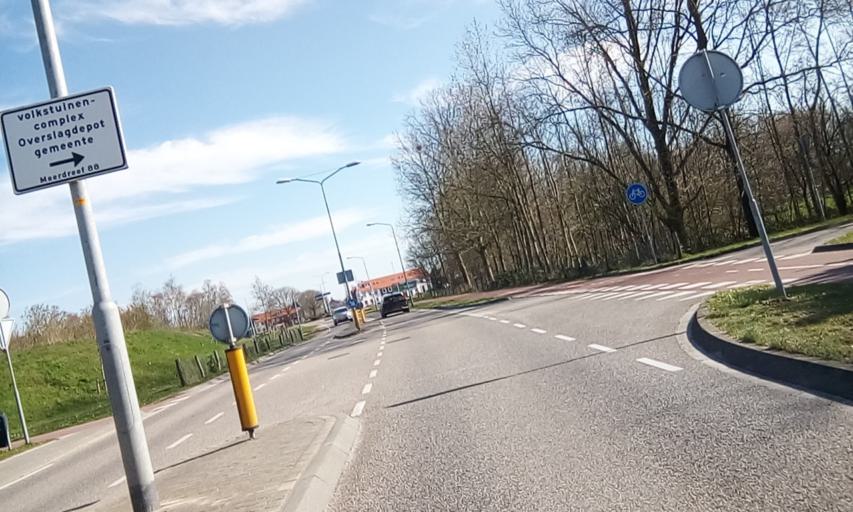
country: NL
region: Gelderland
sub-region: Gemeente Wijchen
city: Wijchen
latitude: 51.8012
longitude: 5.7360
